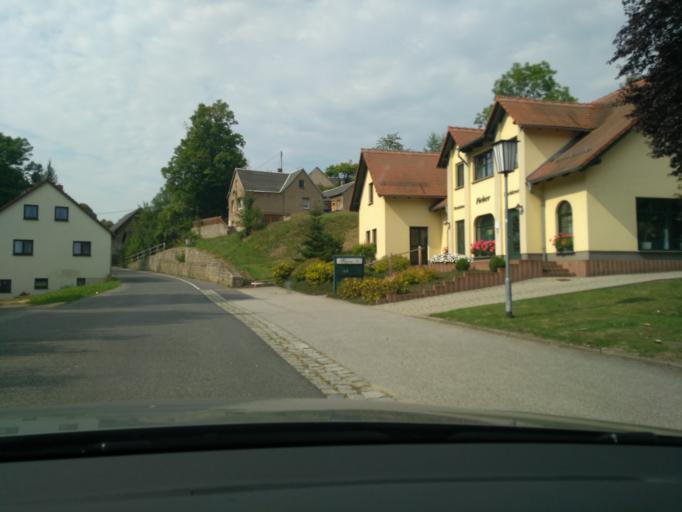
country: DE
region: Saxony
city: Markersdorf
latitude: 51.1444
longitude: 14.8796
